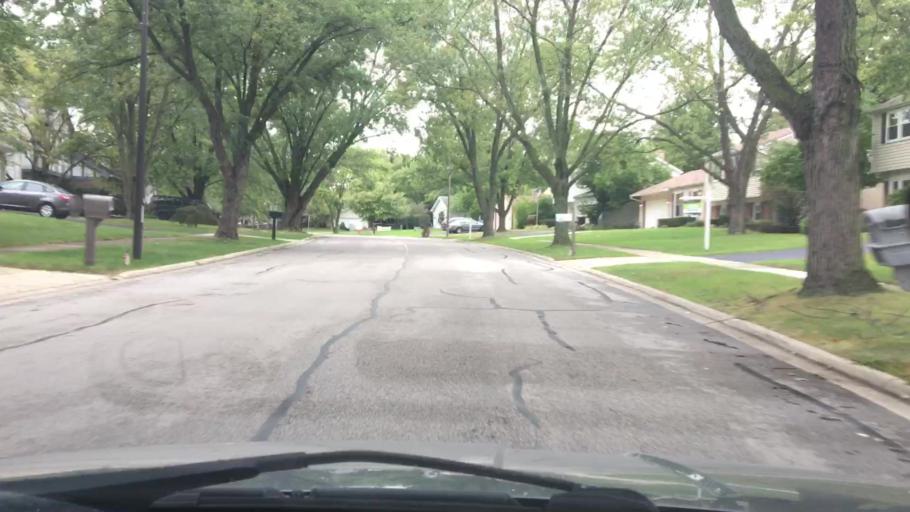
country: US
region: Illinois
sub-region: DuPage County
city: Naperville
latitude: 41.7334
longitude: -88.1344
